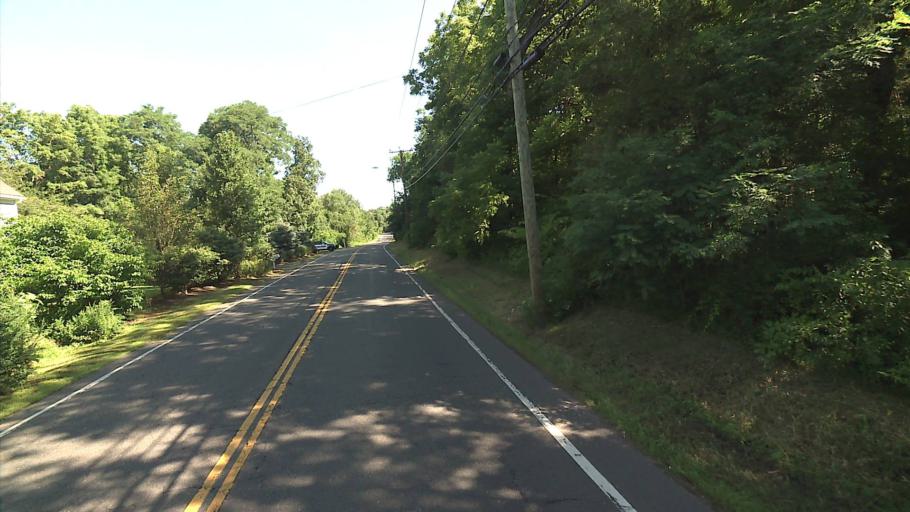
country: US
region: Connecticut
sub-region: Hartford County
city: Farmington
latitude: 41.7503
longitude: -72.8192
